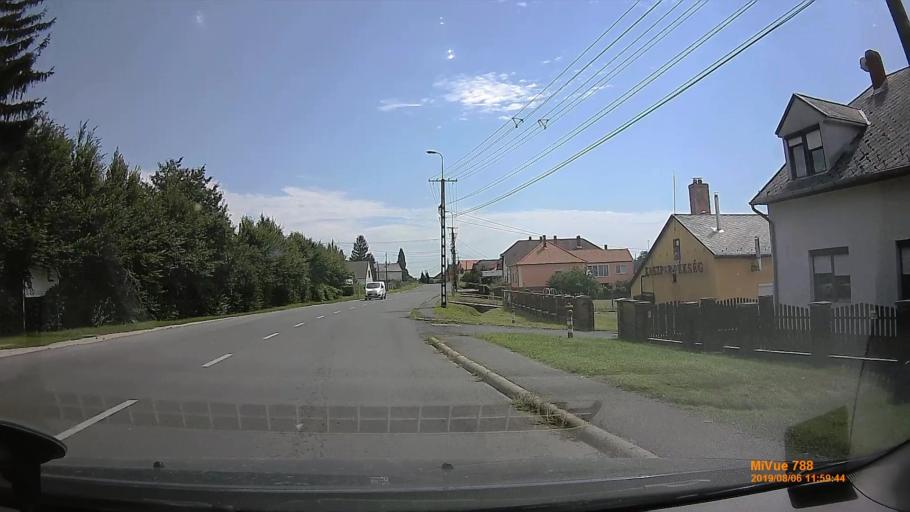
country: HU
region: Zala
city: Becsehely
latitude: 46.4478
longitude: 16.7827
